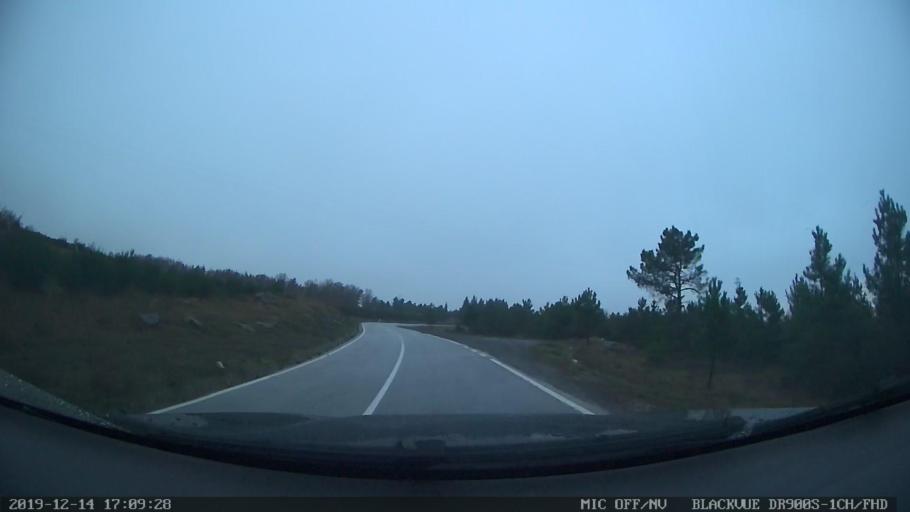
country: PT
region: Vila Real
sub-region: Vila Pouca de Aguiar
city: Vila Pouca de Aguiar
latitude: 41.4765
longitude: -7.6033
